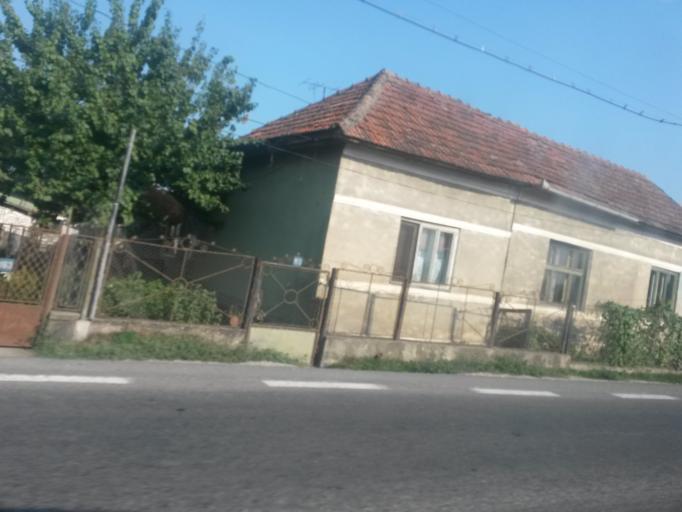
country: RO
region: Alba
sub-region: Comuna Unirea
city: Unirea
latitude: 46.3975
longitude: 23.8090
